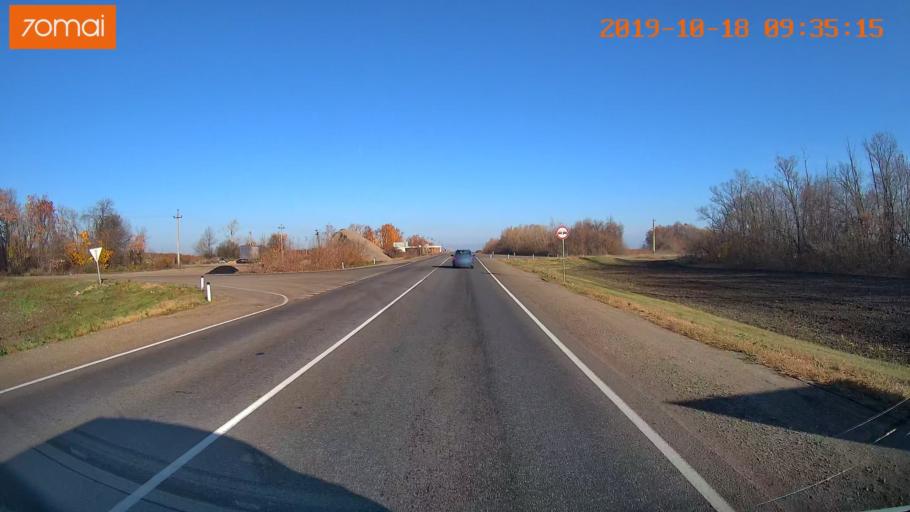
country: RU
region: Tula
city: Yefremov
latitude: 53.1900
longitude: 38.1492
